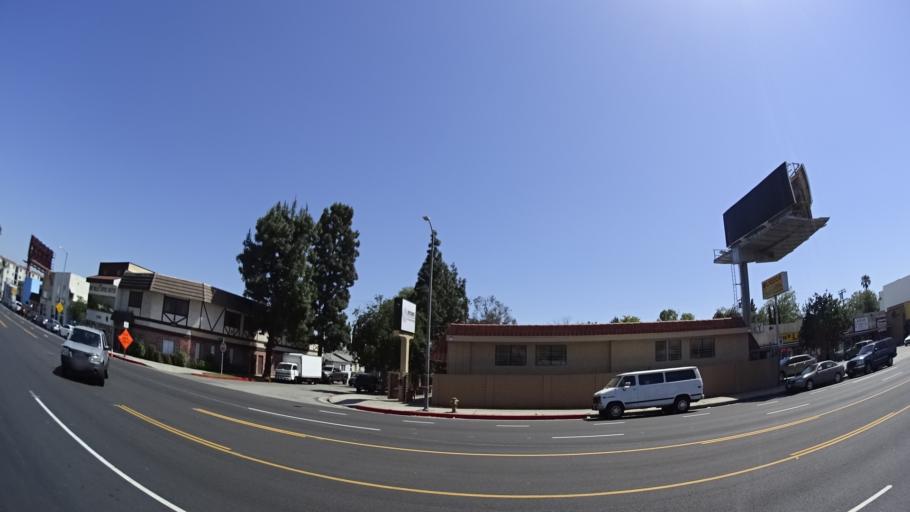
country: US
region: California
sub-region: Los Angeles County
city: North Hollywood
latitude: 34.1722
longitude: -118.3825
